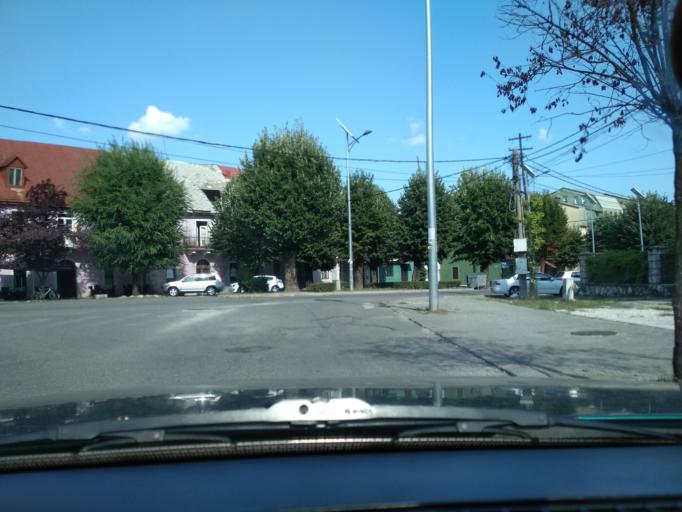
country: ME
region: Cetinje
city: Cetinje
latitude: 42.3941
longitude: 18.9163
